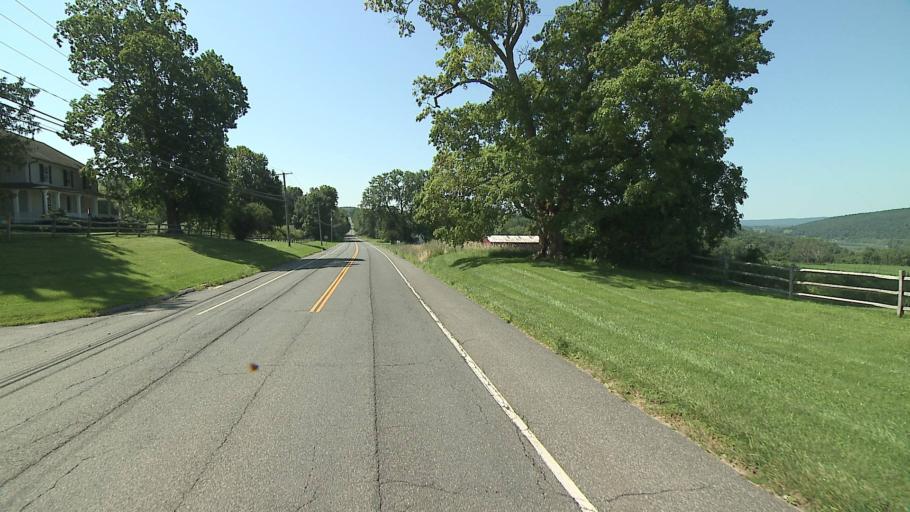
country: US
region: Connecticut
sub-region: Litchfield County
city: Canaan
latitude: 41.9180
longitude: -73.4454
